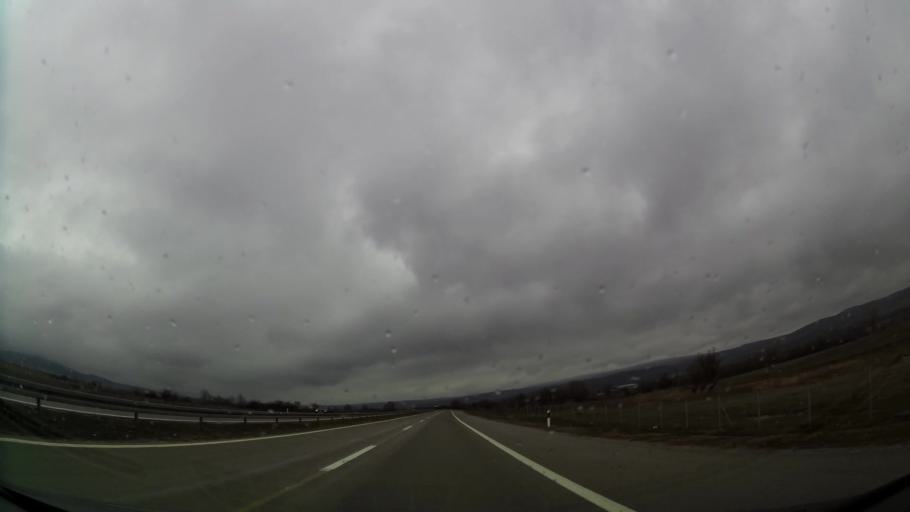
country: RS
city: Zujince
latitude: 42.3144
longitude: 21.7143
